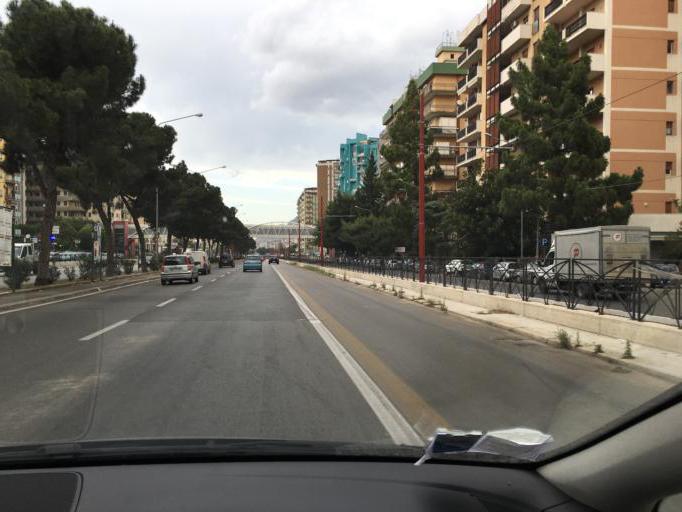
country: IT
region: Sicily
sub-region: Palermo
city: Palermo
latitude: 38.1235
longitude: 13.3292
